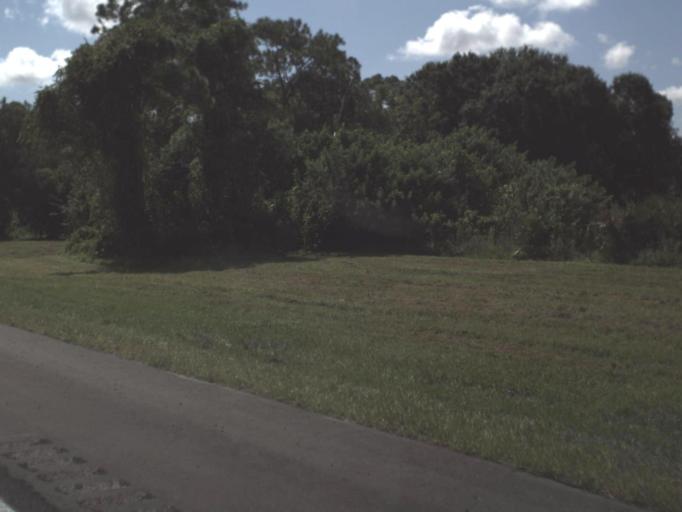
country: US
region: Florida
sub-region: Lee County
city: Tice
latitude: 26.7214
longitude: -81.8195
